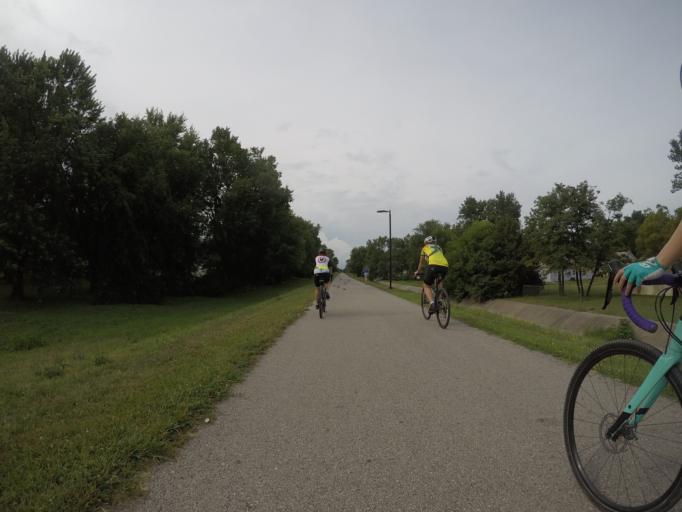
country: US
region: Kansas
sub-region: Franklin County
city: Ottawa
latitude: 38.6081
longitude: -95.2700
